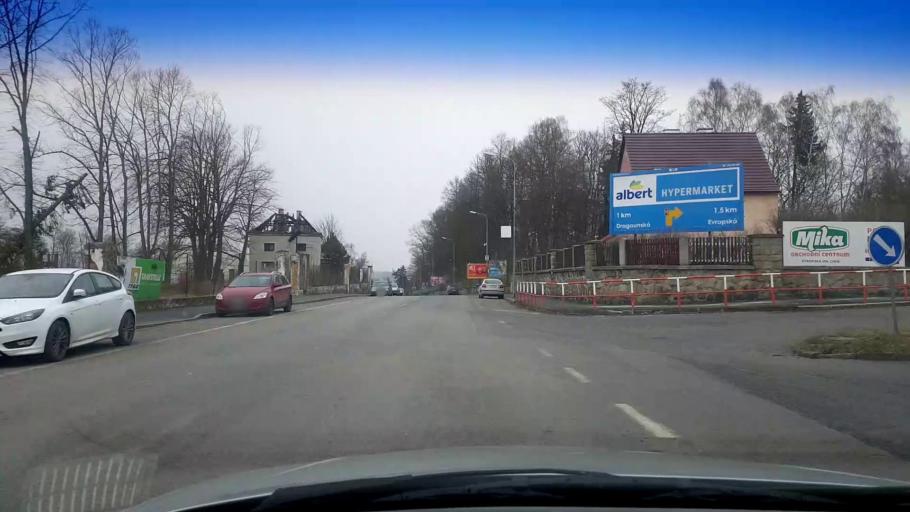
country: CZ
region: Karlovarsky
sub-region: Okres Cheb
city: Cheb
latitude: 50.0688
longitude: 12.3626
